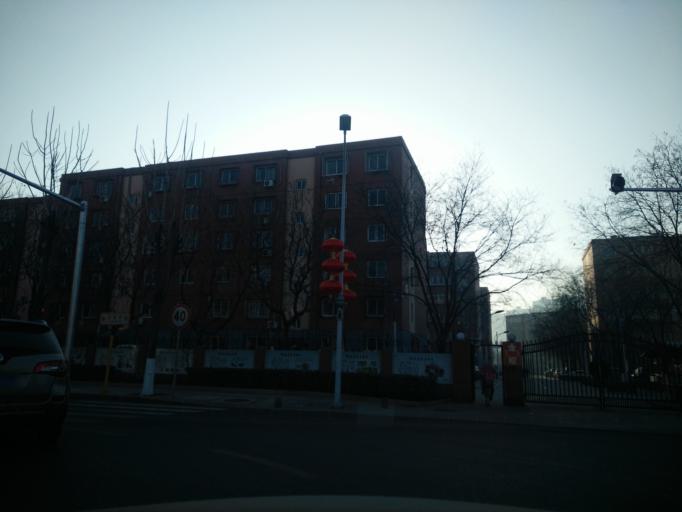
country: CN
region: Beijing
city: Jiugong
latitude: 39.7917
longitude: 116.4754
